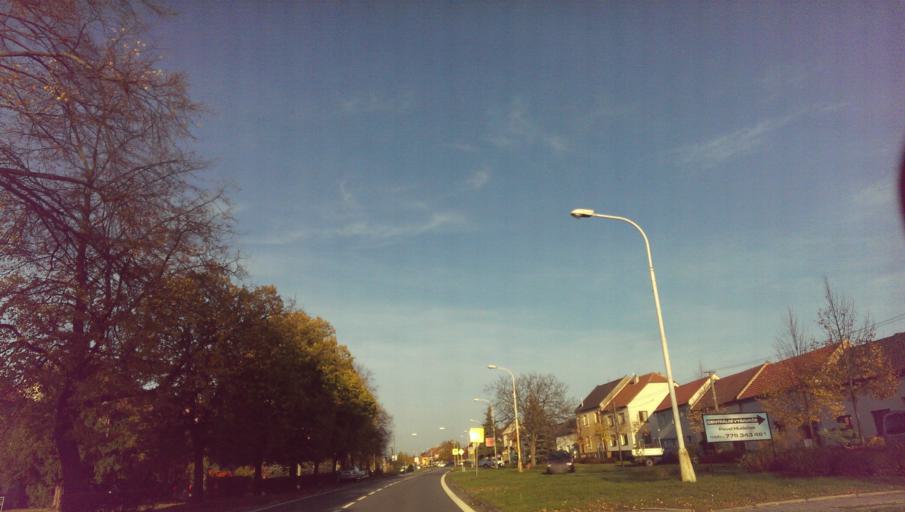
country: CZ
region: Zlin
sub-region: Okres Zlin
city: Ostrozska Nova Ves
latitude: 49.0062
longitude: 17.4363
